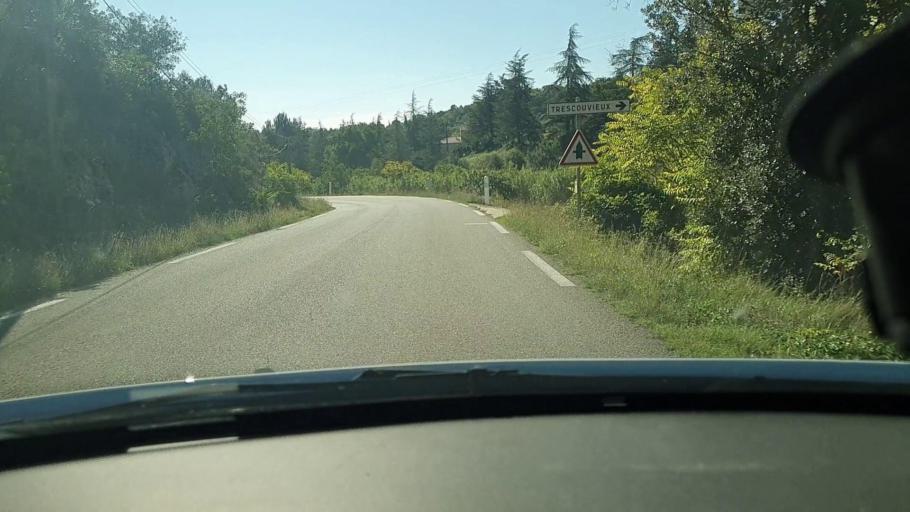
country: FR
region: Languedoc-Roussillon
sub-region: Departement du Gard
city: Saint-Julien-de-Peyrolas
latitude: 44.2972
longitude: 4.5227
